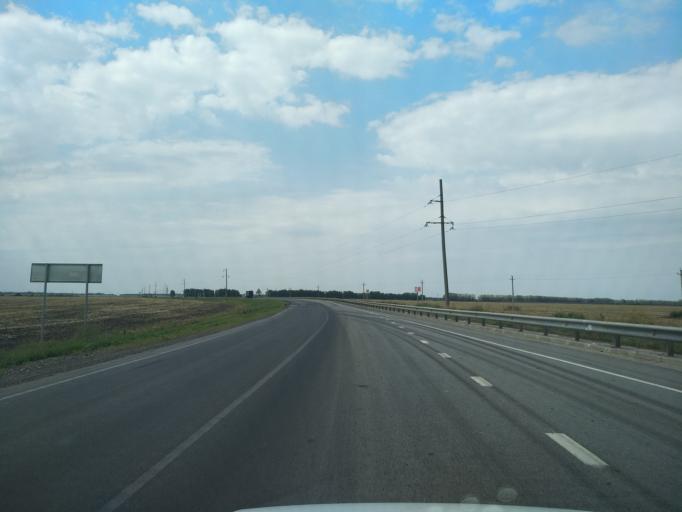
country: RU
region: Voronezj
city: Pereleshino
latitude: 51.8013
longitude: 40.1546
